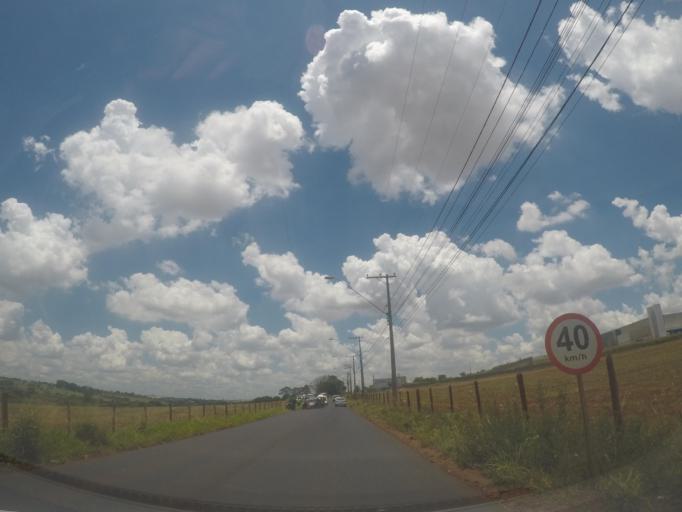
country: BR
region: Sao Paulo
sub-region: Hortolandia
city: Hortolandia
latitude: -22.8212
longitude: -47.2259
